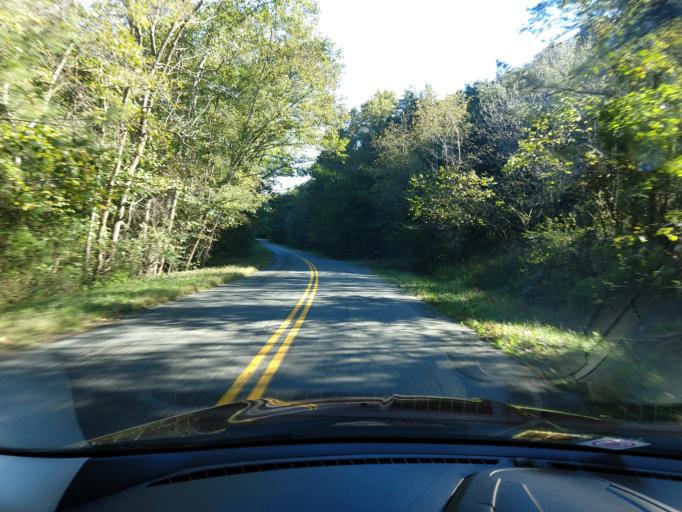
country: US
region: Virginia
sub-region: Alleghany County
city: Clifton Forge
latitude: 37.8376
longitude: -79.8465
